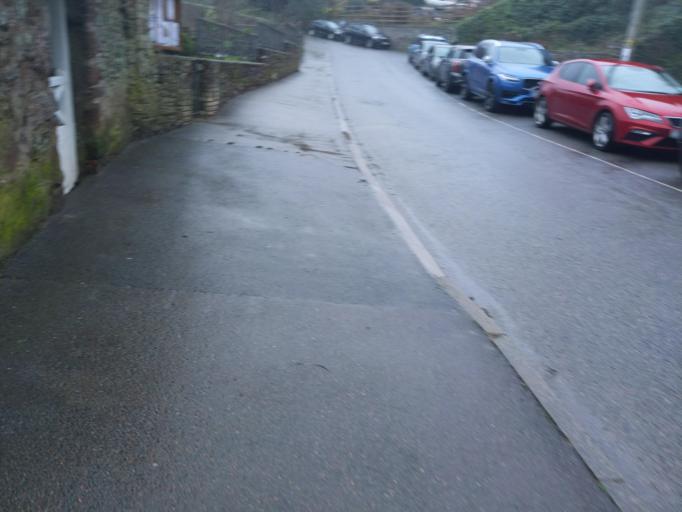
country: GB
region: England
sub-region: Cornwall
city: Millbrook
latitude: 50.3353
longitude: -4.2020
